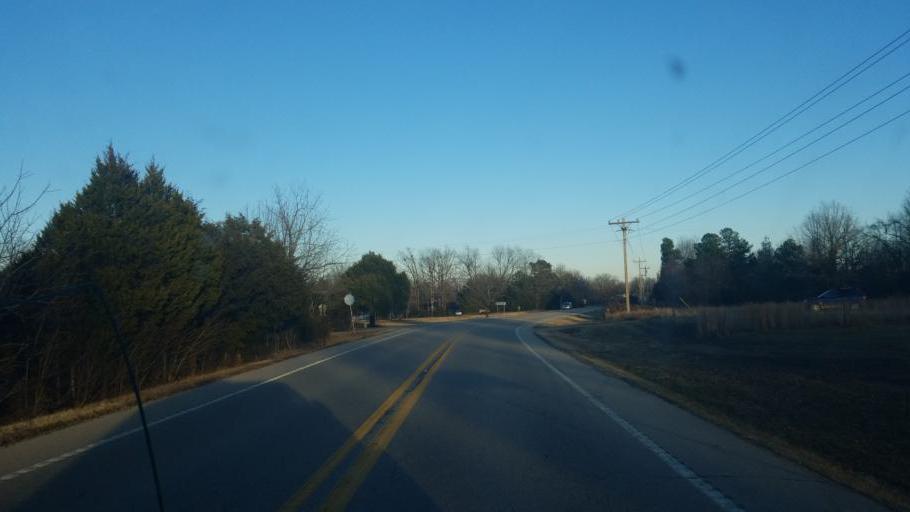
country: US
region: Arkansas
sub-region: Baxter County
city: Mountain Home
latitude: 36.3845
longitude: -92.1661
